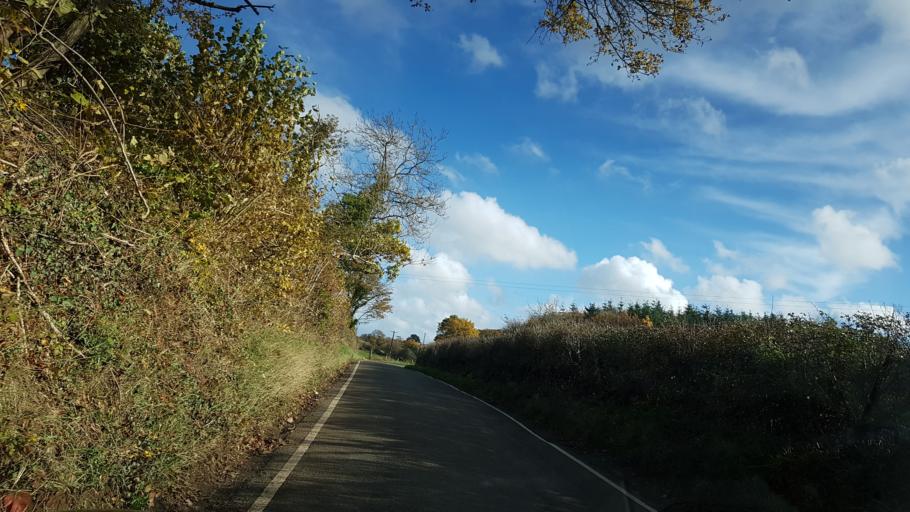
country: GB
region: England
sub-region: Surrey
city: Seale
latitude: 51.2217
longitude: -0.6914
